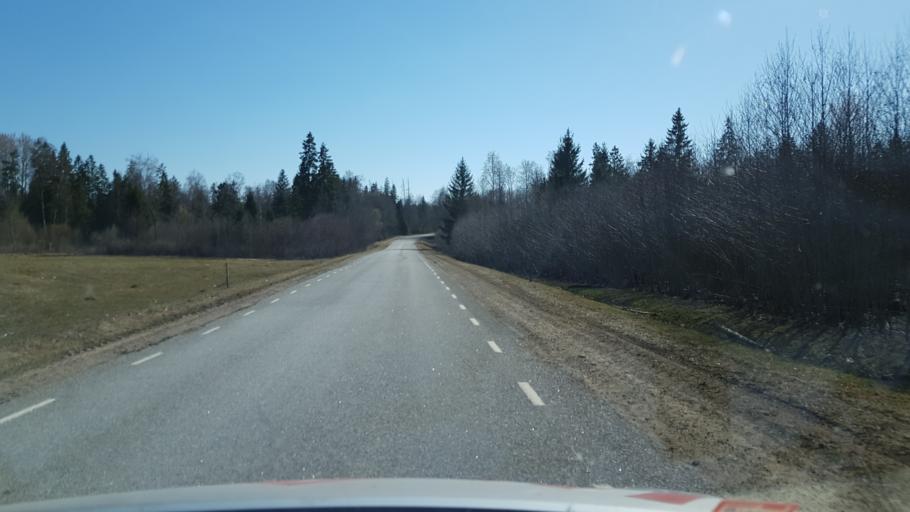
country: EE
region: Laeaene-Virumaa
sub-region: Tamsalu vald
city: Tamsalu
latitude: 59.0589
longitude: 26.1024
